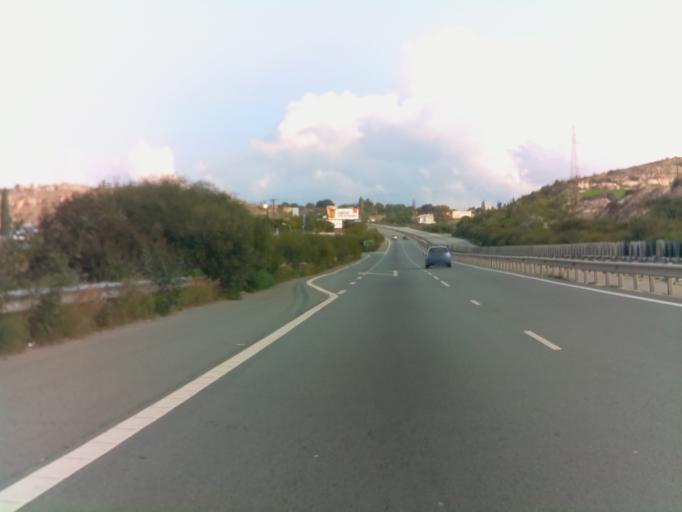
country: CY
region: Larnaka
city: Kofinou
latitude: 34.7935
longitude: 33.3454
